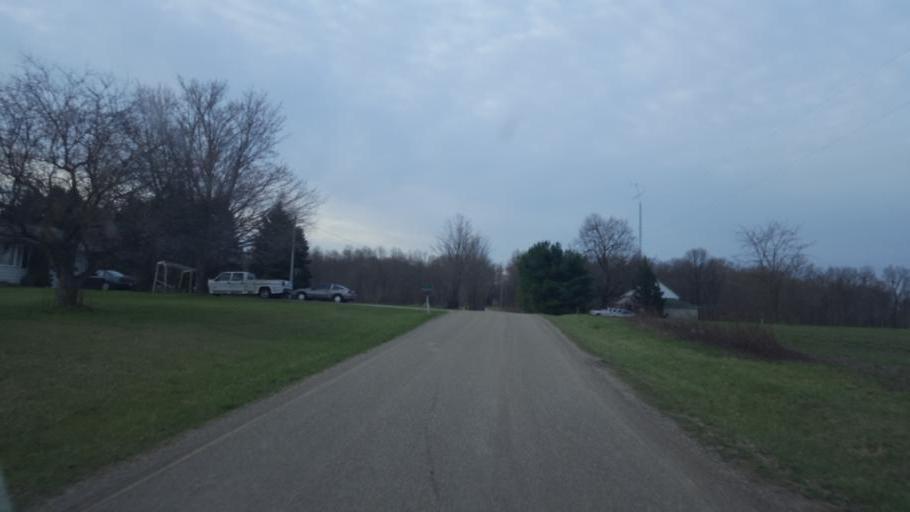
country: US
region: Ohio
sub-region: Sandusky County
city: Bellville
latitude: 40.5747
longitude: -82.5804
